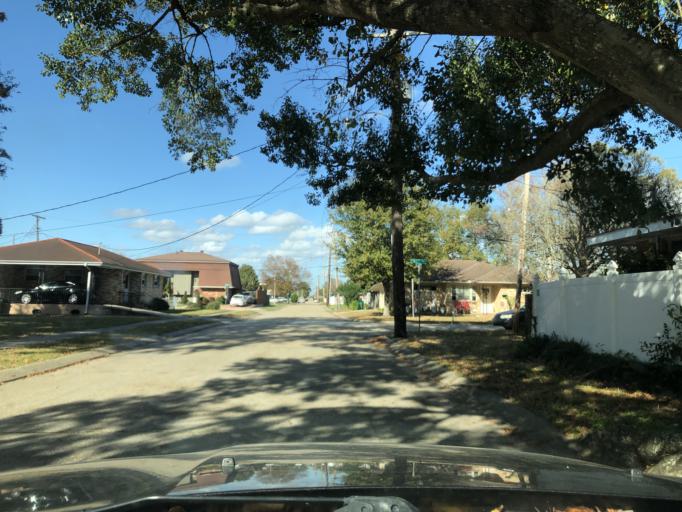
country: US
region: Louisiana
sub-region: Jefferson Parish
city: Metairie Terrace
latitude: 29.9867
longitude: -90.1613
